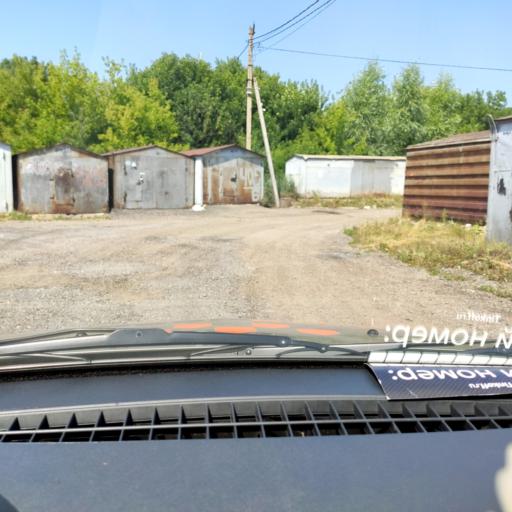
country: RU
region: Bashkortostan
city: Ufa
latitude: 54.7922
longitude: 56.0951
